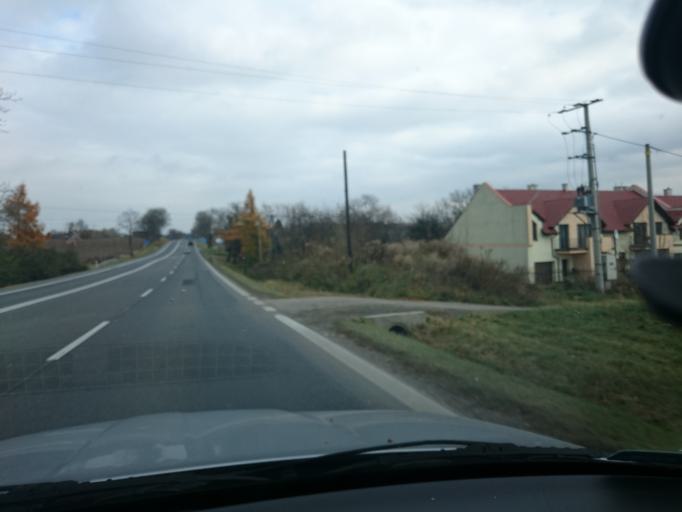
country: PL
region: Lesser Poland Voivodeship
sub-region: Powiat krakowski
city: Michalowice
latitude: 50.1827
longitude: 19.9942
